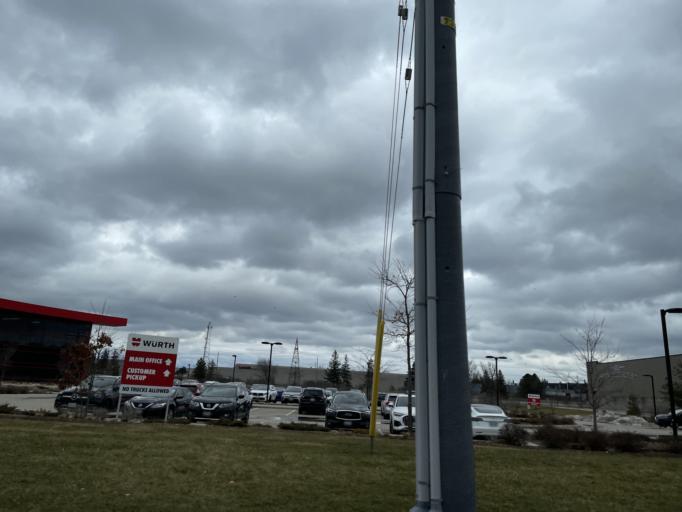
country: CA
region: Ontario
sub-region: Wellington County
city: Guelph
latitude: 43.4940
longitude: -80.2207
